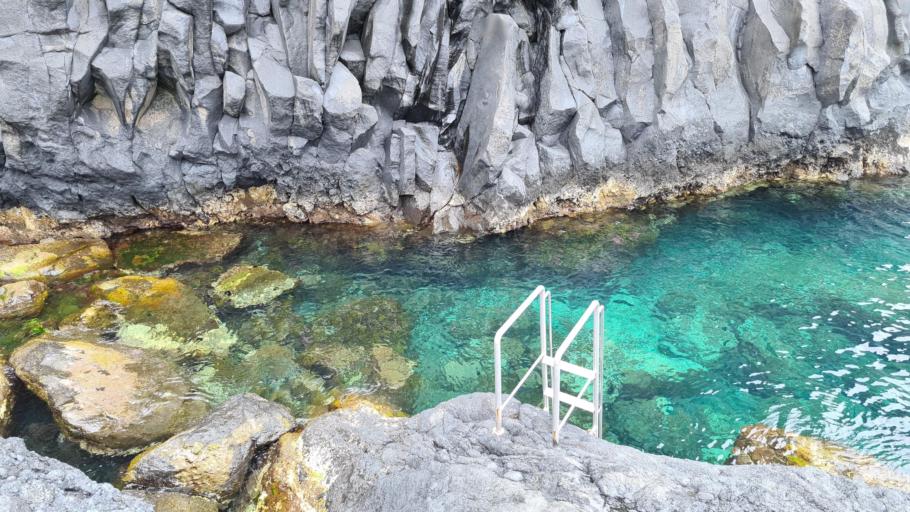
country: PT
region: Azores
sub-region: Sao Roque do Pico
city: Sao Roque do Pico
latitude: 38.6793
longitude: -28.0532
